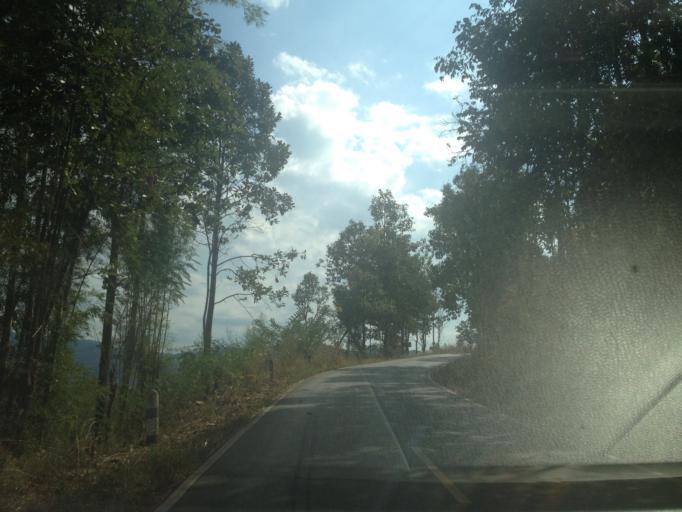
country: TH
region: Mae Hong Son
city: Ban Huai I Huak
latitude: 18.1182
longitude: 98.2183
